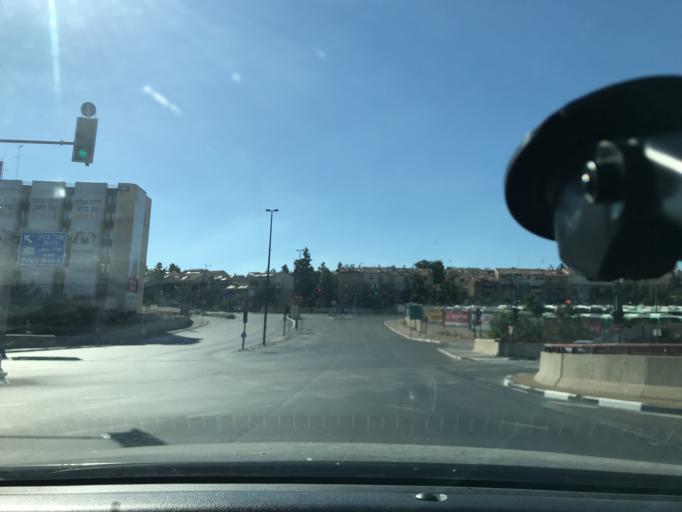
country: IL
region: Jerusalem
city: West Jerusalem
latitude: 31.7849
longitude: 35.1995
